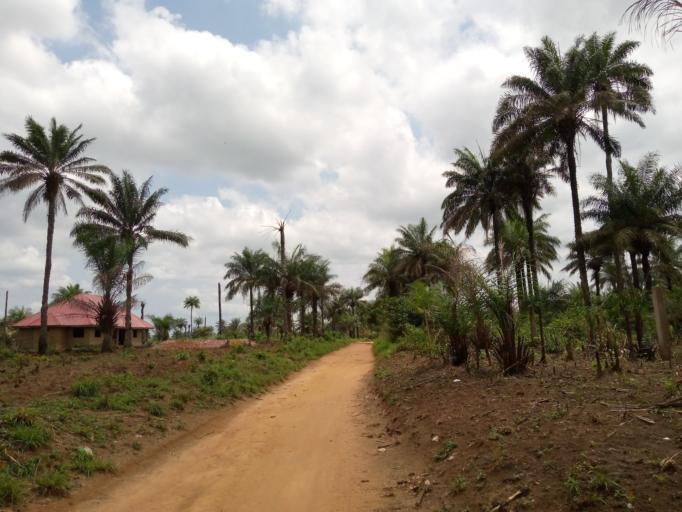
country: SL
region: Western Area
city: Waterloo
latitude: 8.3991
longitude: -12.9469
